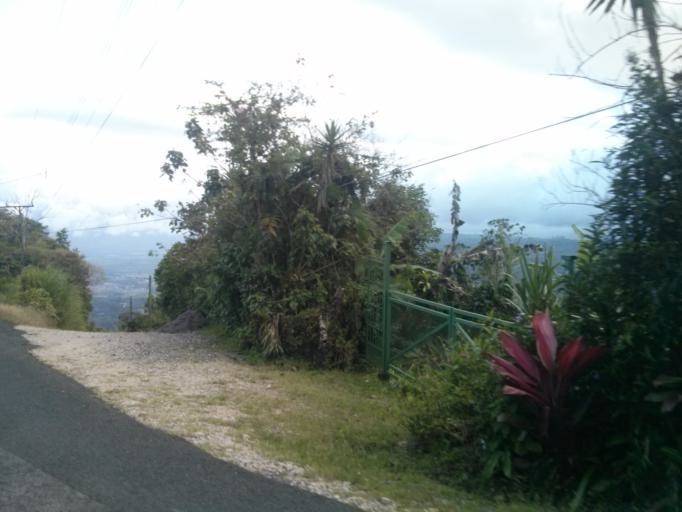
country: CR
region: Cartago
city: Turrialba
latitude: 9.9537
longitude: -83.7119
